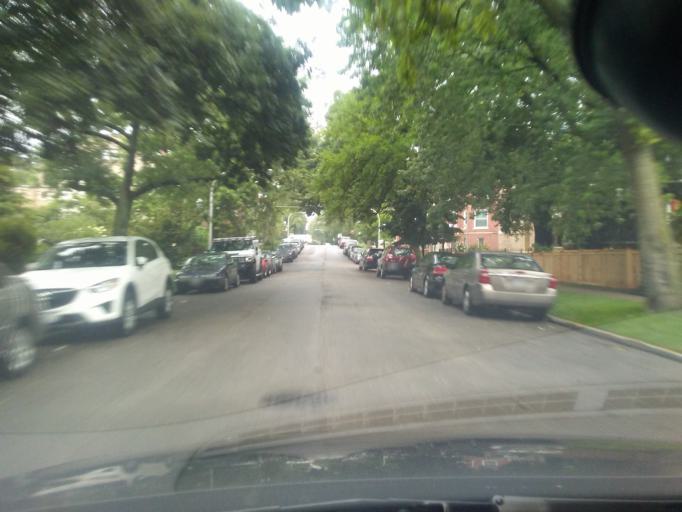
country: US
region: Illinois
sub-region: Cook County
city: Evanston
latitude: 42.0113
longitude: -87.6813
